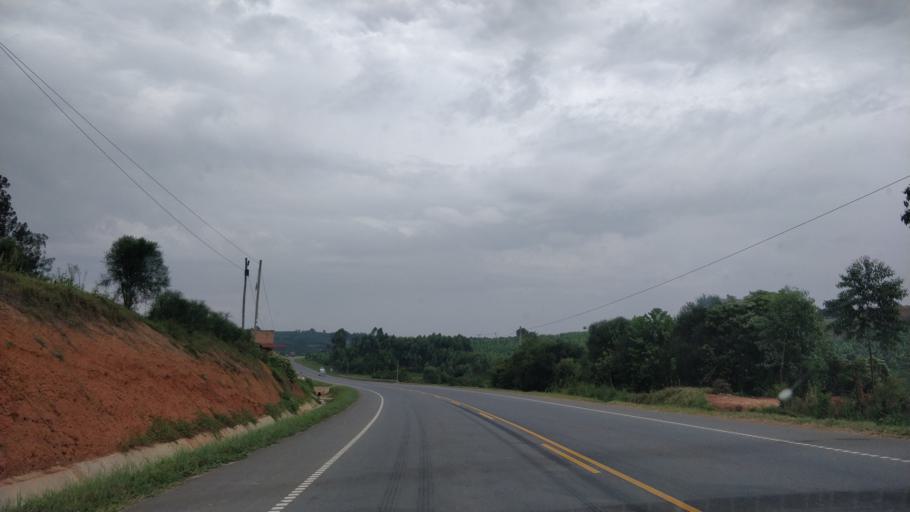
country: UG
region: Western Region
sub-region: Sheema District
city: Kibingo
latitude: -0.6543
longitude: 30.4826
